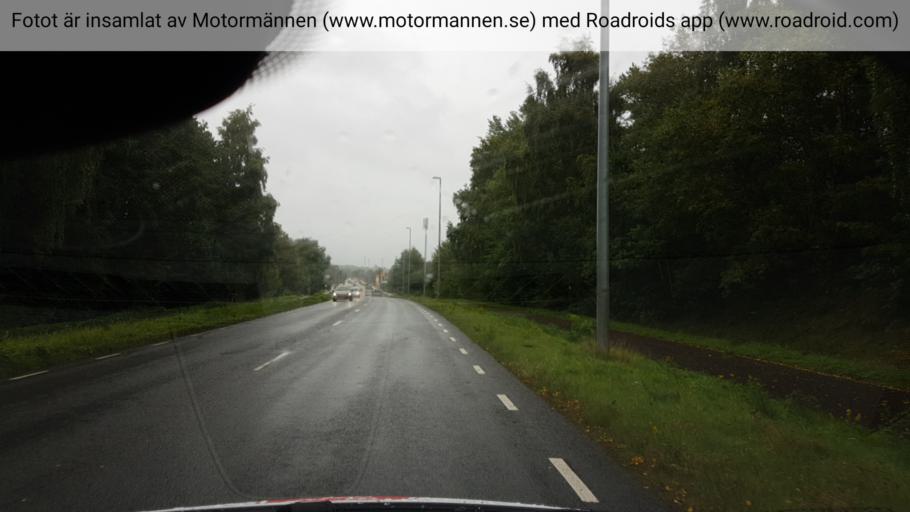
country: SE
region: Halland
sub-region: Halmstads Kommun
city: Mjallby
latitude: 56.6570
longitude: 12.8006
